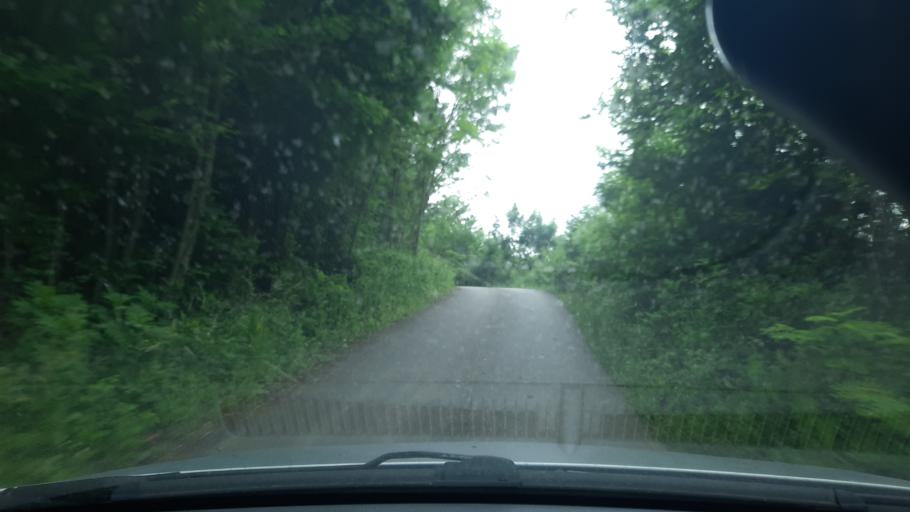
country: RS
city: Jarebice
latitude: 44.5141
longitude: 19.4779
